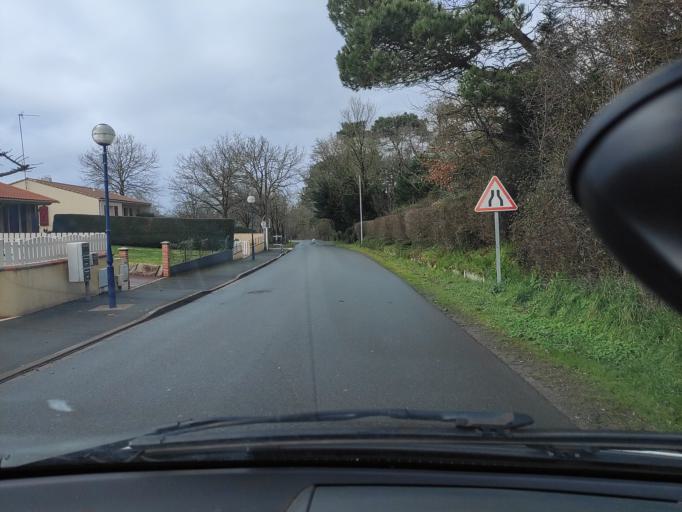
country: FR
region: Pays de la Loire
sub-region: Departement de la Vendee
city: La Boissiere-des-Landes
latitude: 46.5647
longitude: -1.4622
